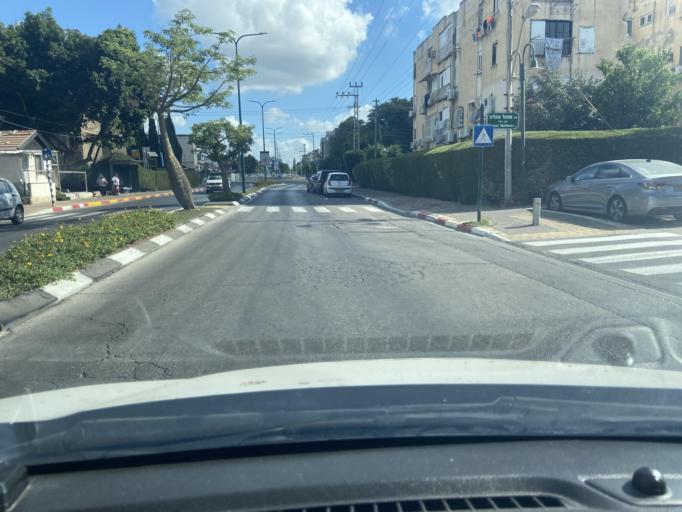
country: IL
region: Central District
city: Yehud
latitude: 32.0305
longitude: 34.8973
